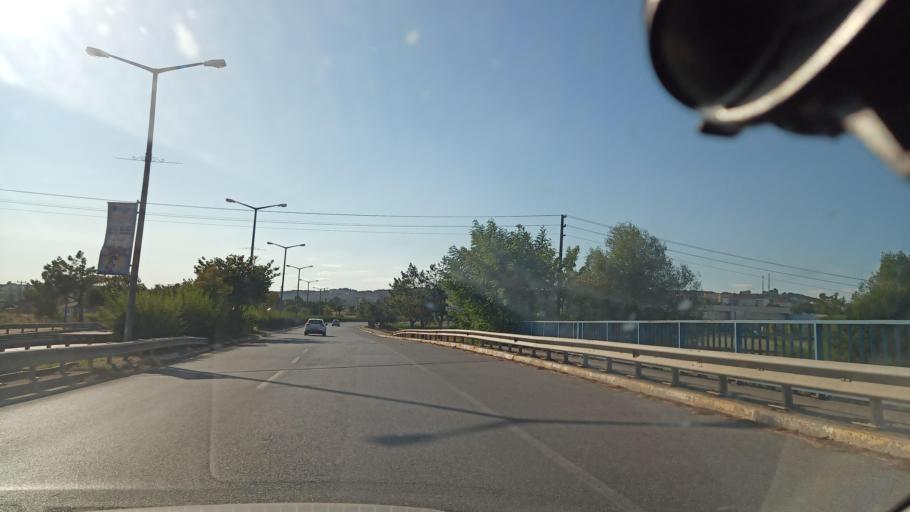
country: TR
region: Sakarya
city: Kazimpasa
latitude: 40.8491
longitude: 30.3218
